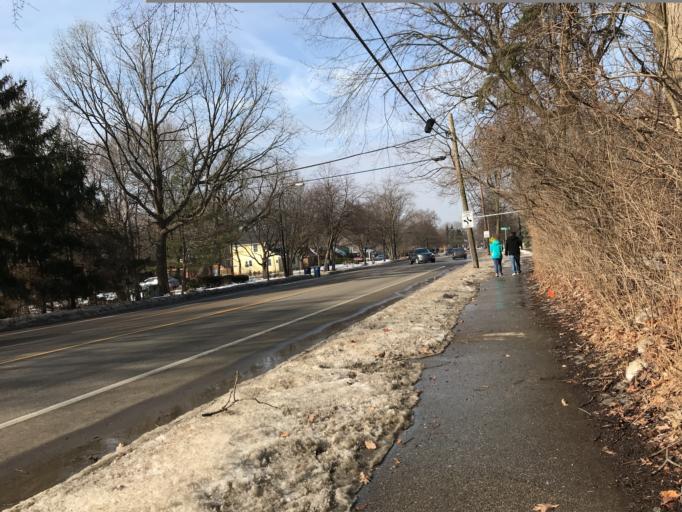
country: US
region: Michigan
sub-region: Washtenaw County
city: Ann Arbor
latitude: 42.2523
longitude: -83.7236
